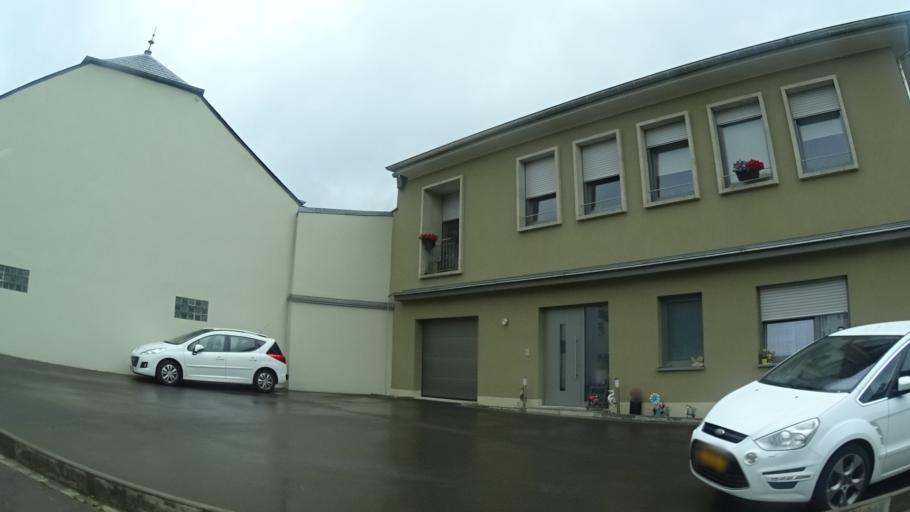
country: LU
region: Luxembourg
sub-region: Canton de Capellen
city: Clemency
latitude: 49.5961
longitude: 5.8761
